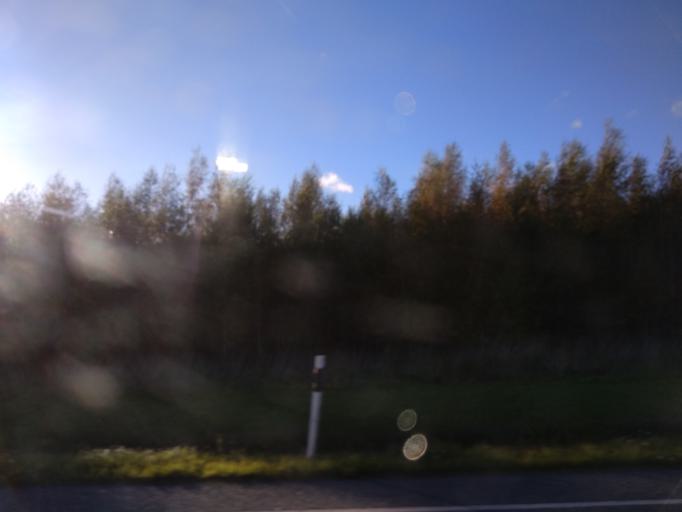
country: EE
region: Polvamaa
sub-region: Polva linn
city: Polva
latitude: 58.0249
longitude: 27.0639
